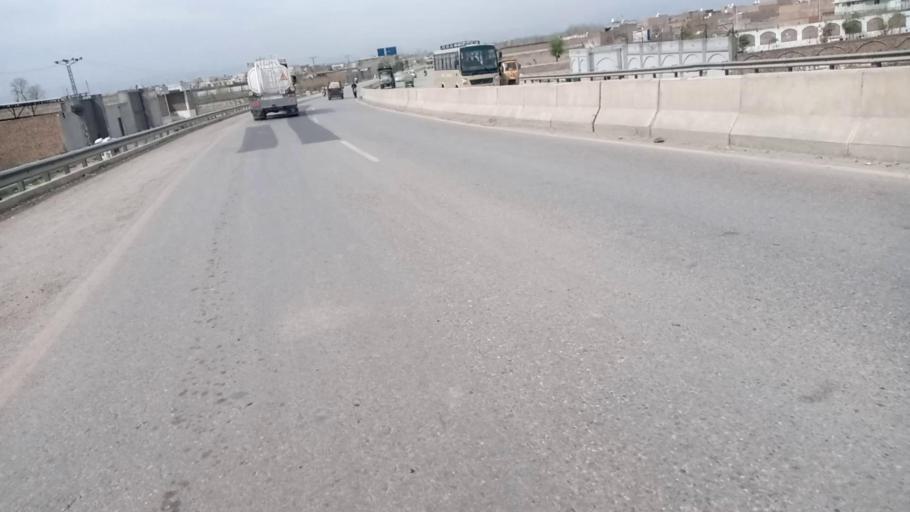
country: PK
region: Khyber Pakhtunkhwa
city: Peshawar
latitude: 34.0396
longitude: 71.6193
